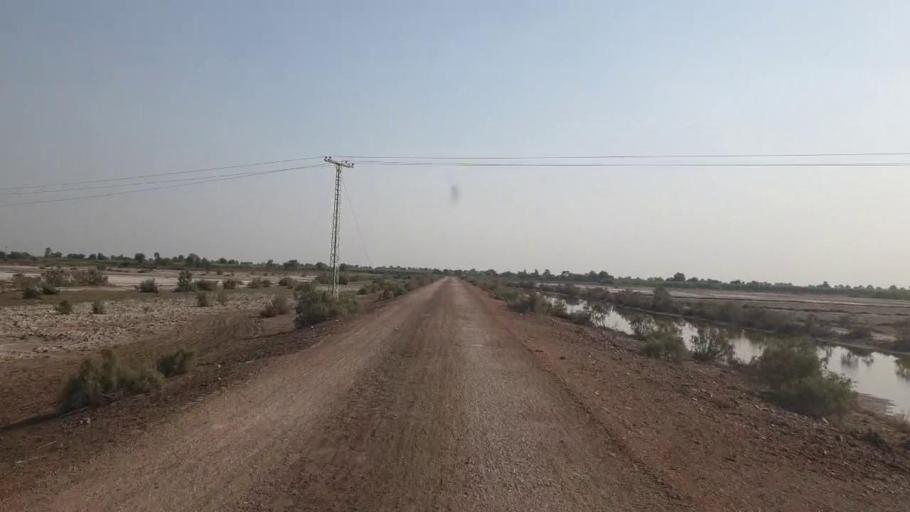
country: PK
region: Sindh
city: Sanghar
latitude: 26.0488
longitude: 68.8972
